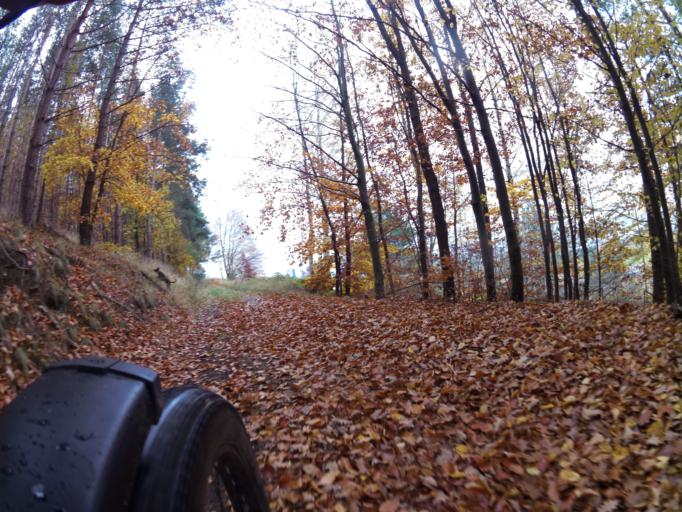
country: PL
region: Pomeranian Voivodeship
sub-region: Powiat wejherowski
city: Gniewino
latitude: 54.7510
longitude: 18.0857
